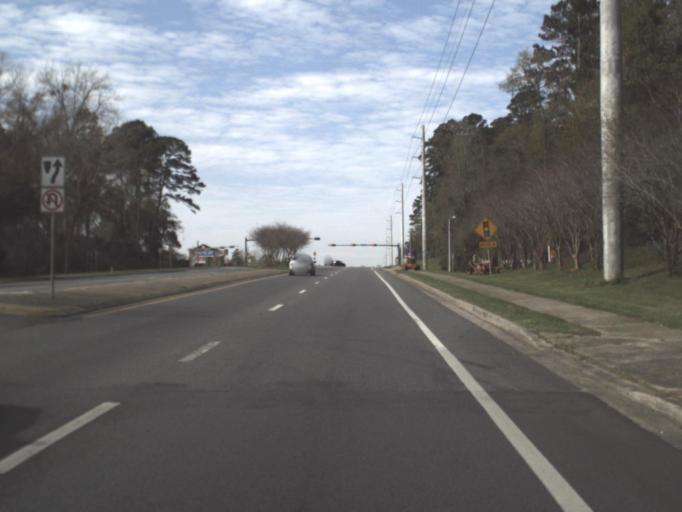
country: US
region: Florida
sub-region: Leon County
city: Tallahassee
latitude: 30.4657
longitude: -84.2126
